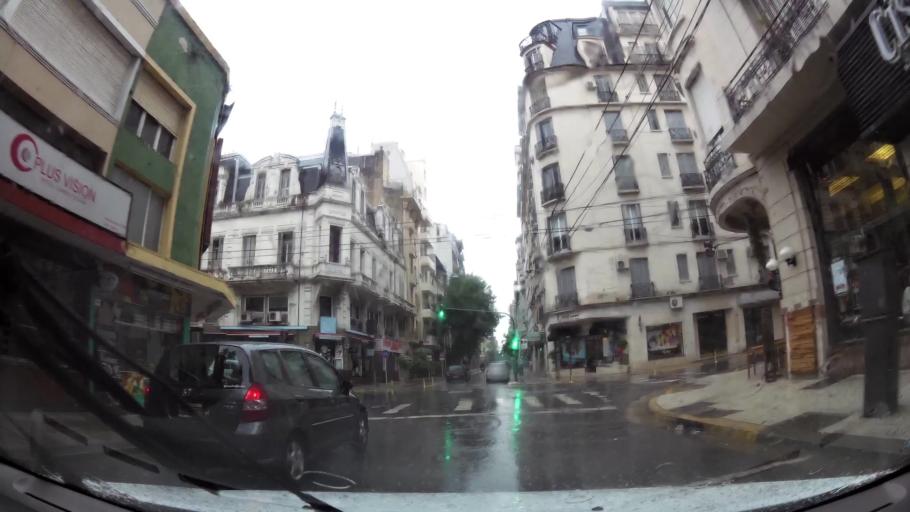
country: AR
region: Buenos Aires F.D.
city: Retiro
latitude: -34.5970
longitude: -58.3899
